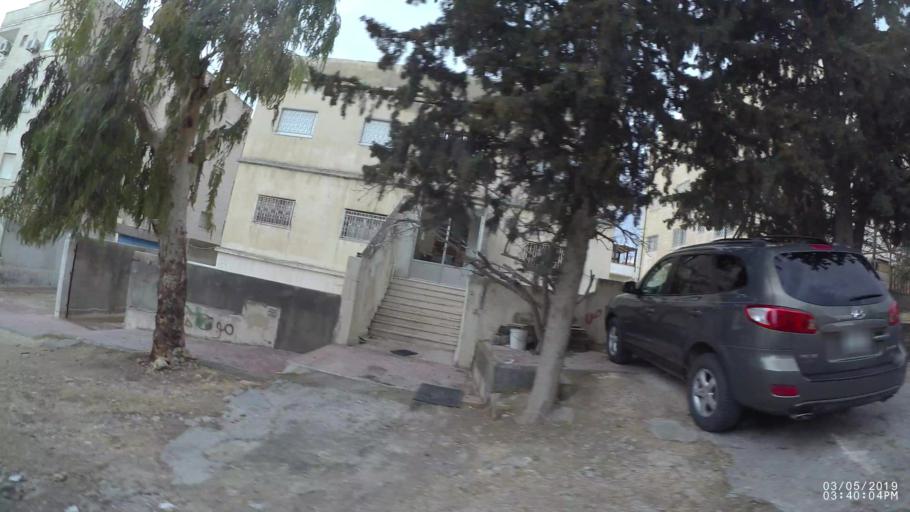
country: JO
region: Amman
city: Amman
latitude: 32.0073
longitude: 35.9428
